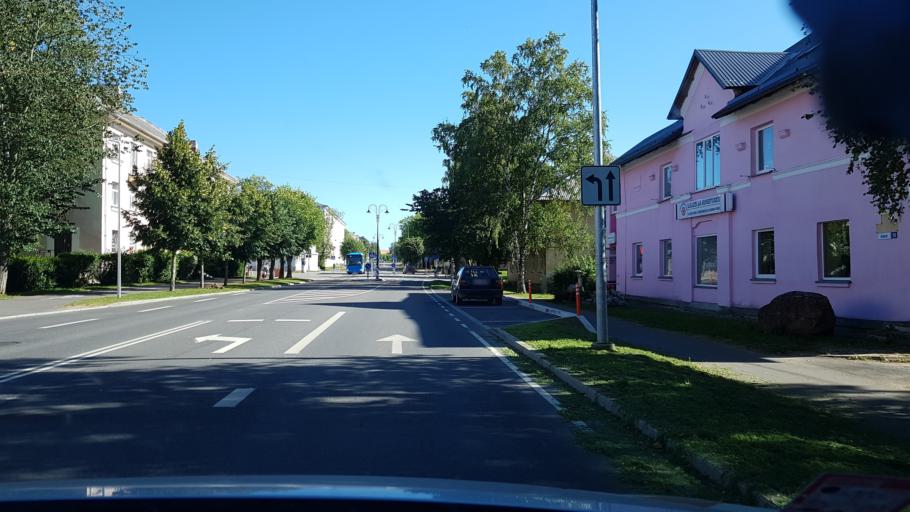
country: EE
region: Ida-Virumaa
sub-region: Kohtla-Jaerve linn
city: Kohtla-Jarve
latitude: 59.4034
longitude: 27.2860
